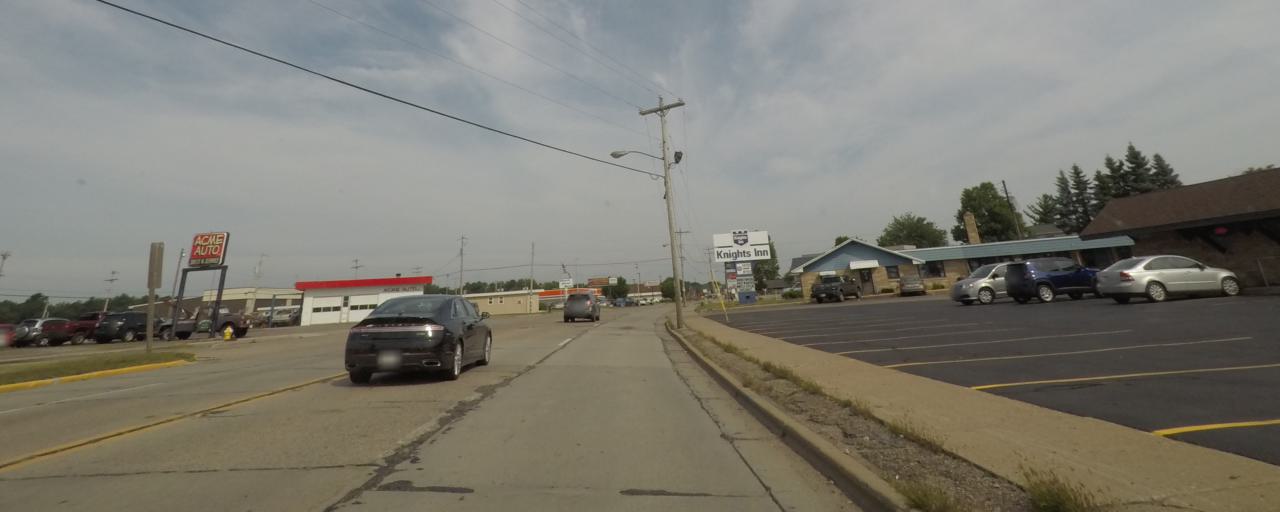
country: US
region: Wisconsin
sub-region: Portage County
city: Whiting
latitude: 44.4987
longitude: -89.5621
